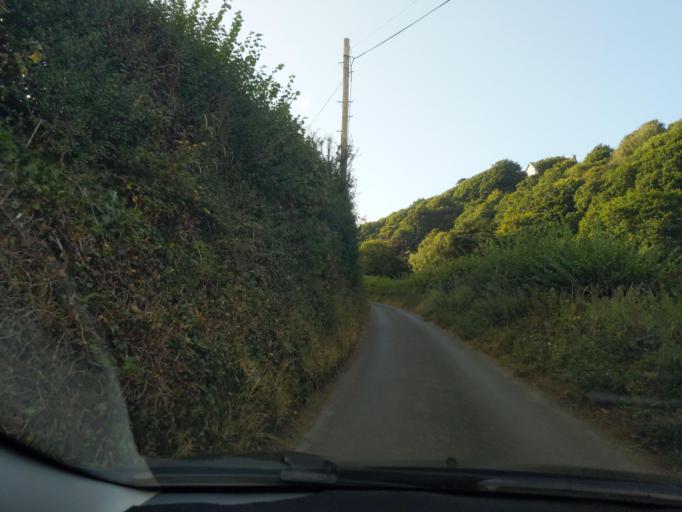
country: GB
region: England
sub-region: Devon
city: Salcombe
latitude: 50.2265
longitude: -3.7902
